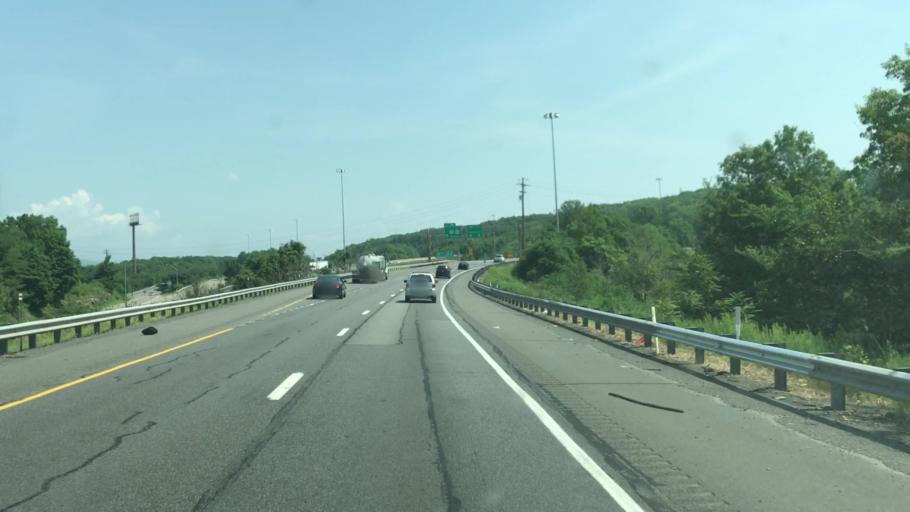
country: US
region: Pennsylvania
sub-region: Lackawanna County
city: Moosic
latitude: 41.3524
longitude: -75.7241
